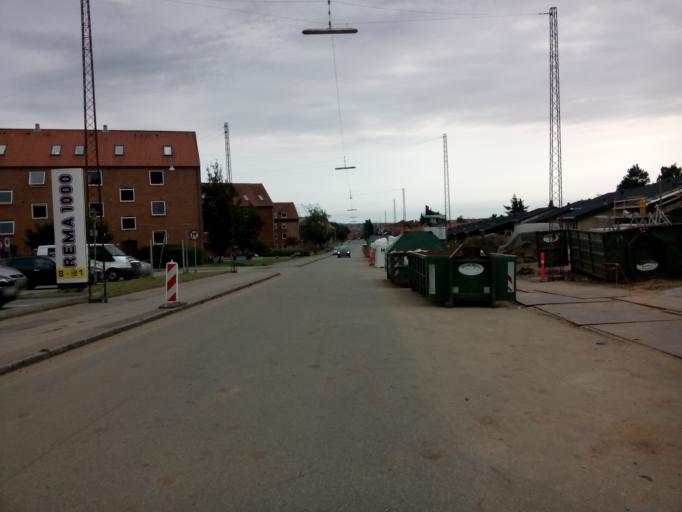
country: DK
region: Central Jutland
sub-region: Arhus Kommune
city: Arhus
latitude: 56.1701
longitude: 10.1845
